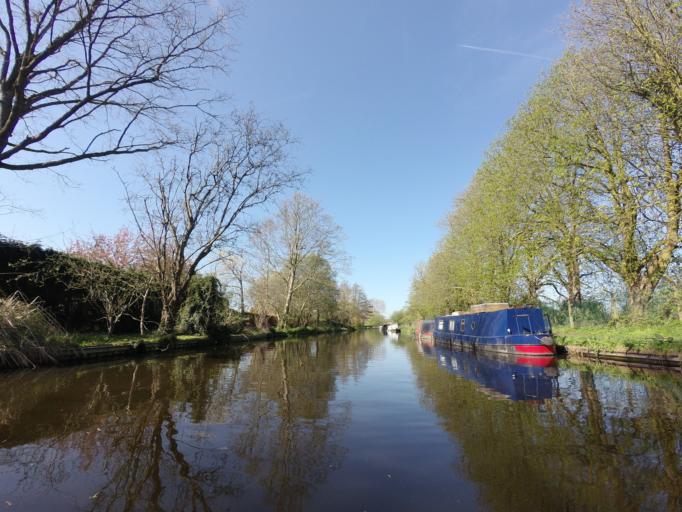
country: GB
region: England
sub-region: Greater London
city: Uxbridge
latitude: 51.5565
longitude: -0.4835
